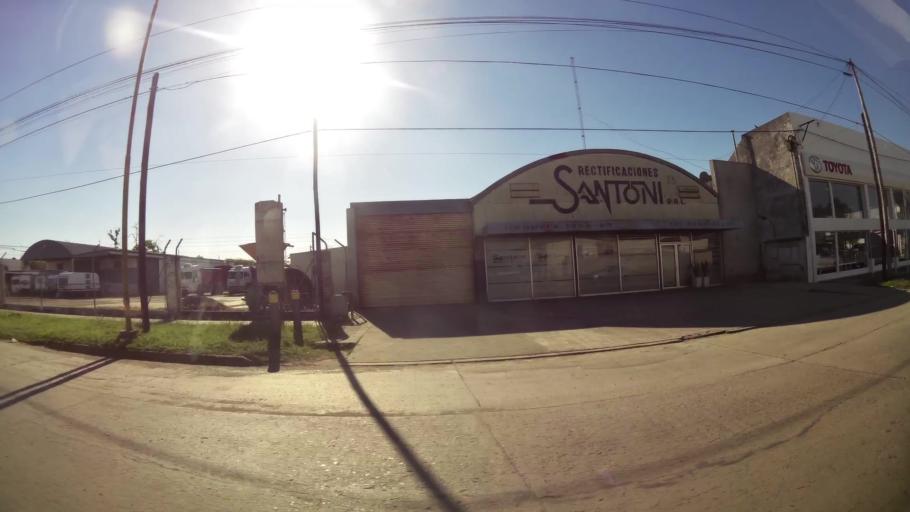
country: AR
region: Cordoba
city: San Francisco
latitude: -31.4153
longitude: -62.0942
